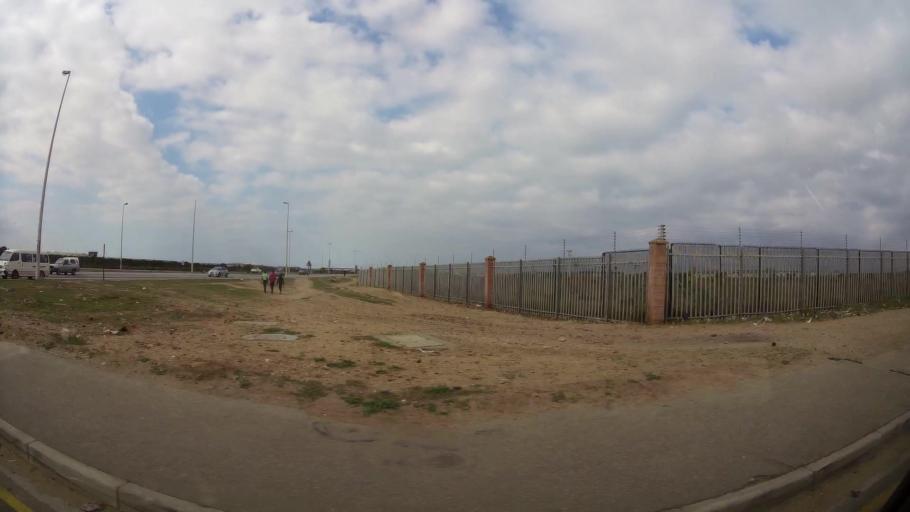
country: ZA
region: Eastern Cape
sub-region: Nelson Mandela Bay Metropolitan Municipality
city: Port Elizabeth
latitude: -33.8211
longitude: 25.6381
